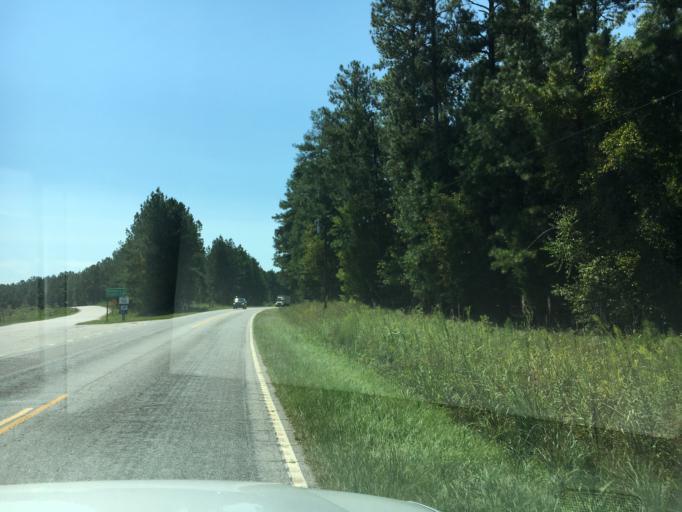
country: US
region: South Carolina
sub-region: Laurens County
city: Joanna
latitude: 34.3140
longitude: -81.8438
